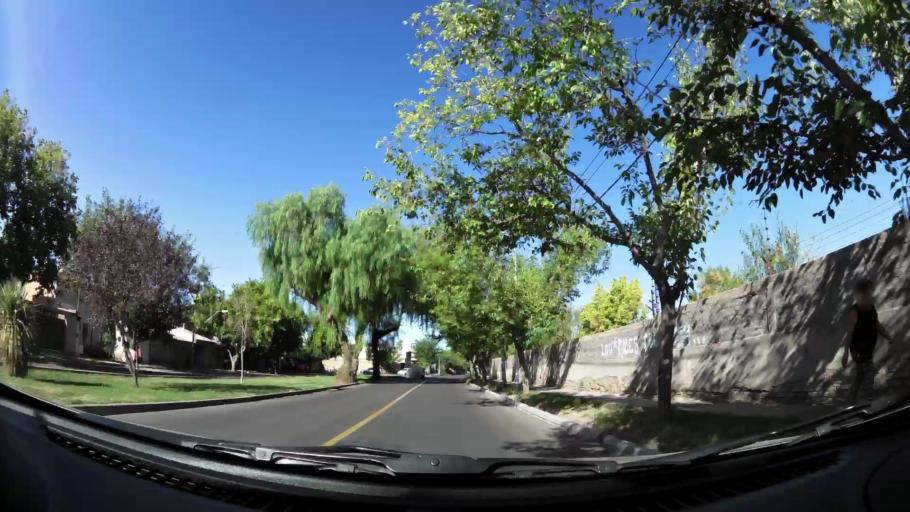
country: AR
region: Mendoza
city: Villa Nueva
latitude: -32.9152
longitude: -68.8009
